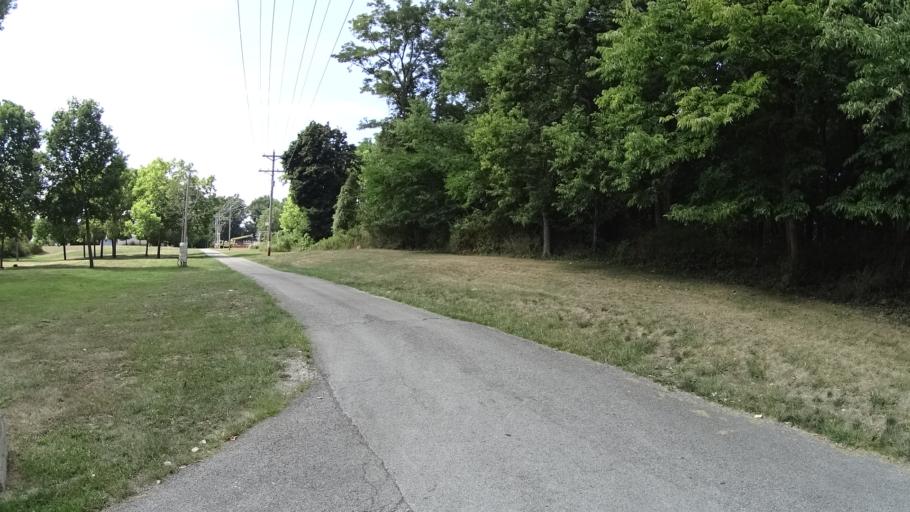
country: US
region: Ohio
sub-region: Erie County
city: Sandusky
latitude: 41.5981
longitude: -82.7220
